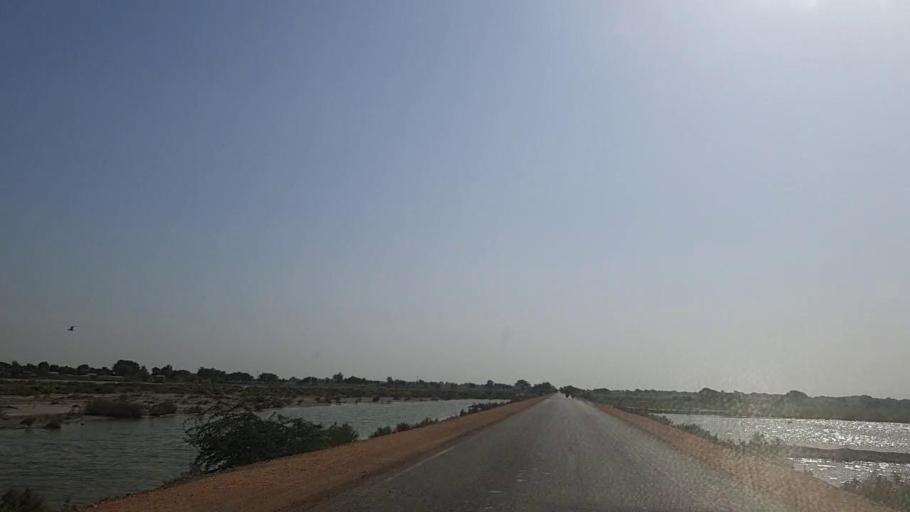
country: PK
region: Sindh
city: Mirpur Batoro
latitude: 24.5801
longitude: 68.2892
